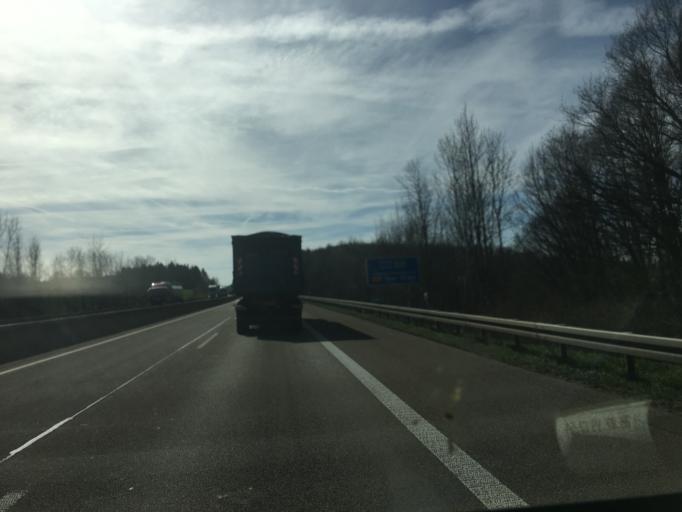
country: DE
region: North Rhine-Westphalia
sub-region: Regierungsbezirk Koln
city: Mechernich
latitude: 50.5664
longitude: 6.6823
